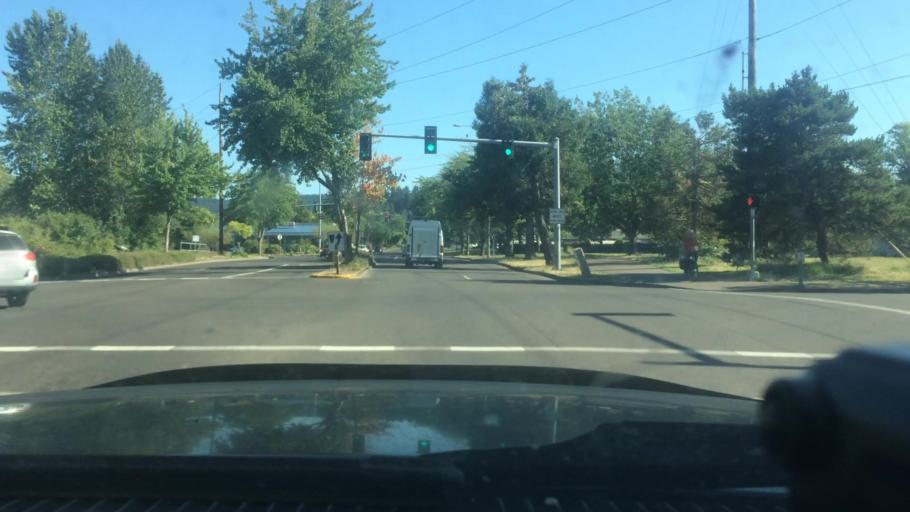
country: US
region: Oregon
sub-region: Lane County
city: Eugene
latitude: 44.0212
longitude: -123.0816
